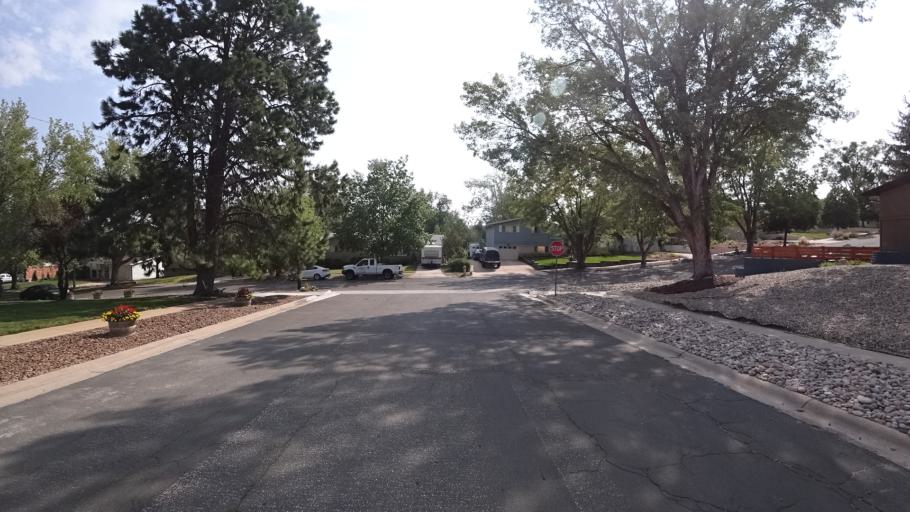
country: US
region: Colorado
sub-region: El Paso County
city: Colorado Springs
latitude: 38.8515
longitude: -104.7860
